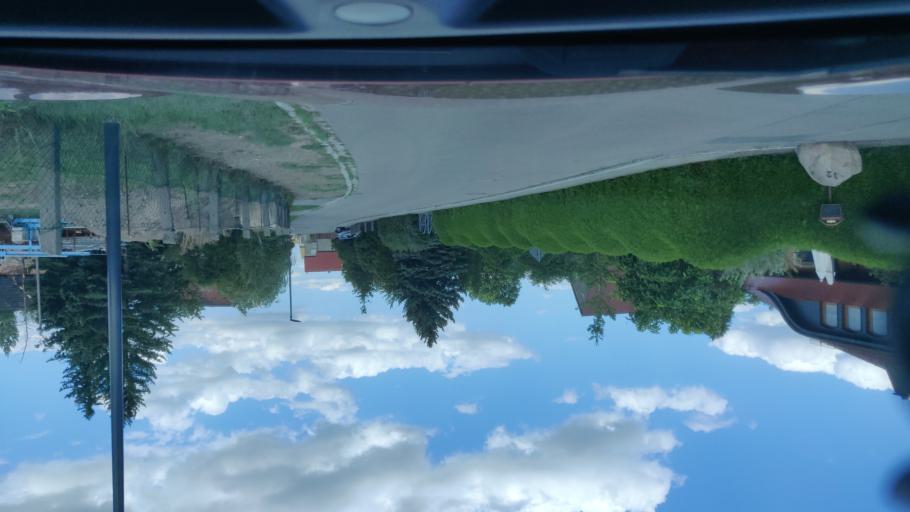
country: DE
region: Saxony
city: Mockrehna
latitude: 51.5048
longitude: 12.8635
